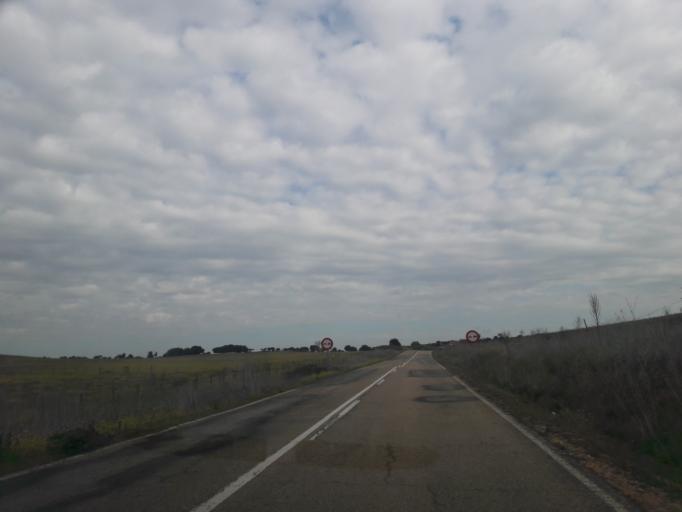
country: ES
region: Castille and Leon
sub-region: Provincia de Salamanca
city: Pastores
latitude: 40.5480
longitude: -6.5284
